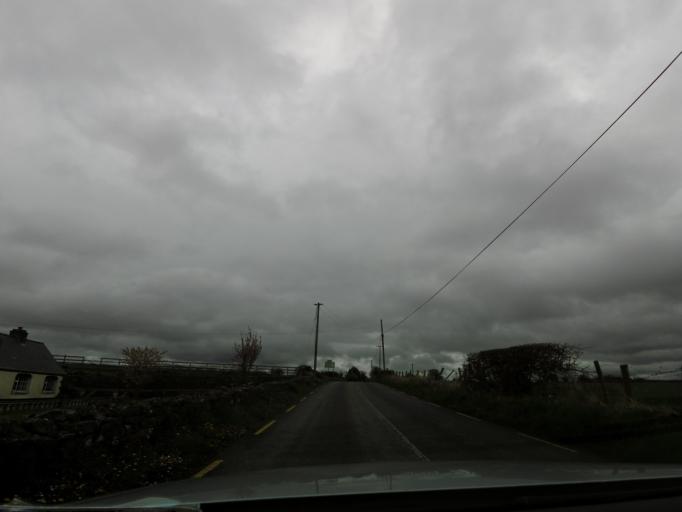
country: IE
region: Leinster
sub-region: Laois
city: Rathdowney
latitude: 52.7238
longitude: -7.5711
